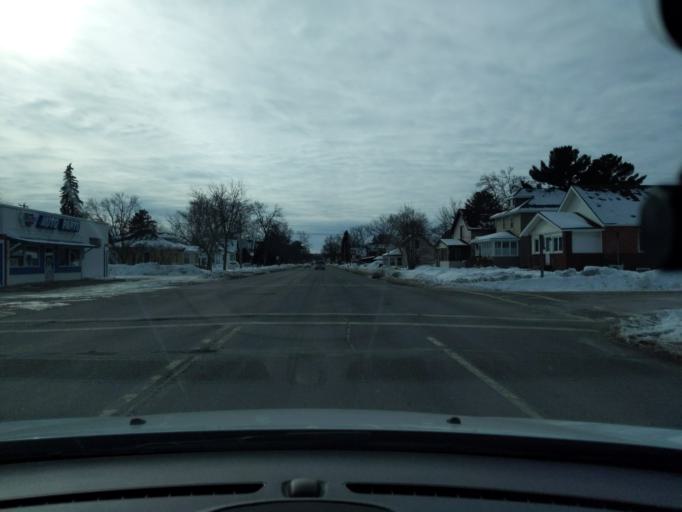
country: US
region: Wisconsin
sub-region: Washburn County
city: Spooner
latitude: 45.8326
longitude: -91.8841
